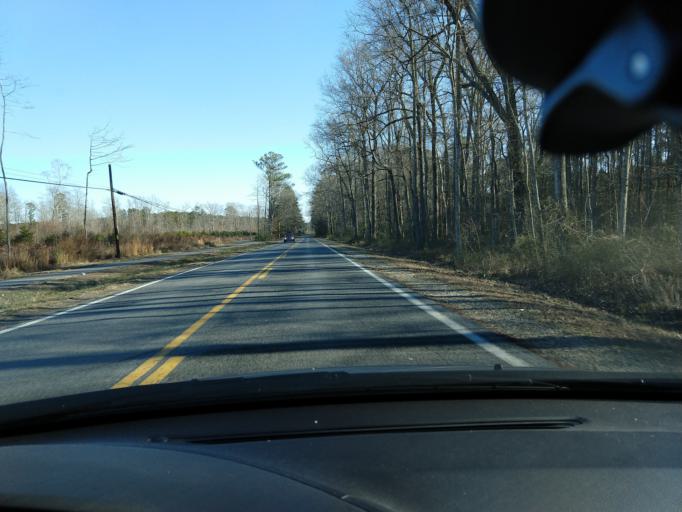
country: US
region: Virginia
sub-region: Charles City County
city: Charles City
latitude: 37.3247
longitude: -76.9806
